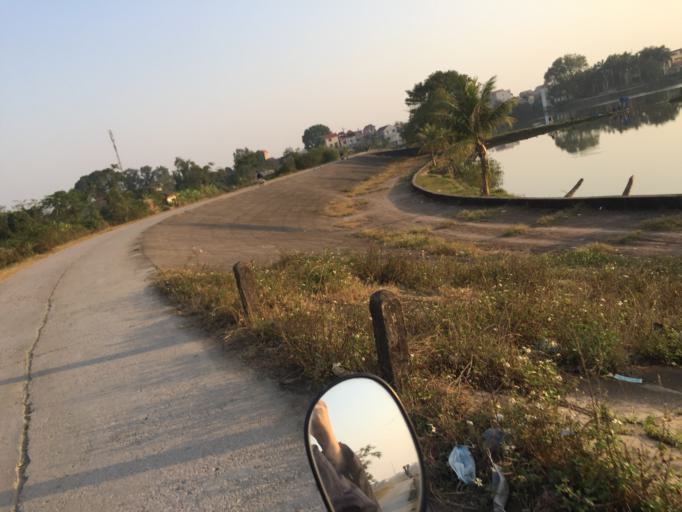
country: VN
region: Ha Noi
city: Chuc Son
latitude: 20.9071
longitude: 105.7152
